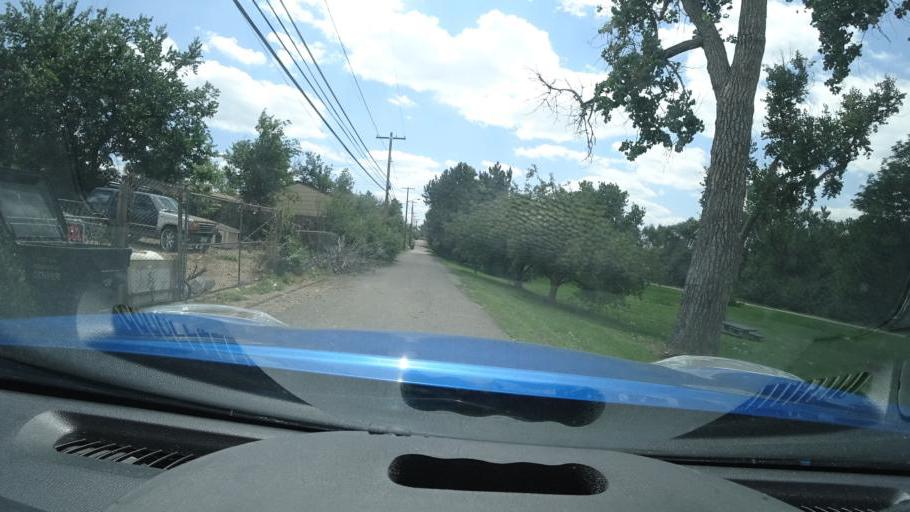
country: US
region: Colorado
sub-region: Arapahoe County
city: Englewood
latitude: 39.6729
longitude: -104.9965
